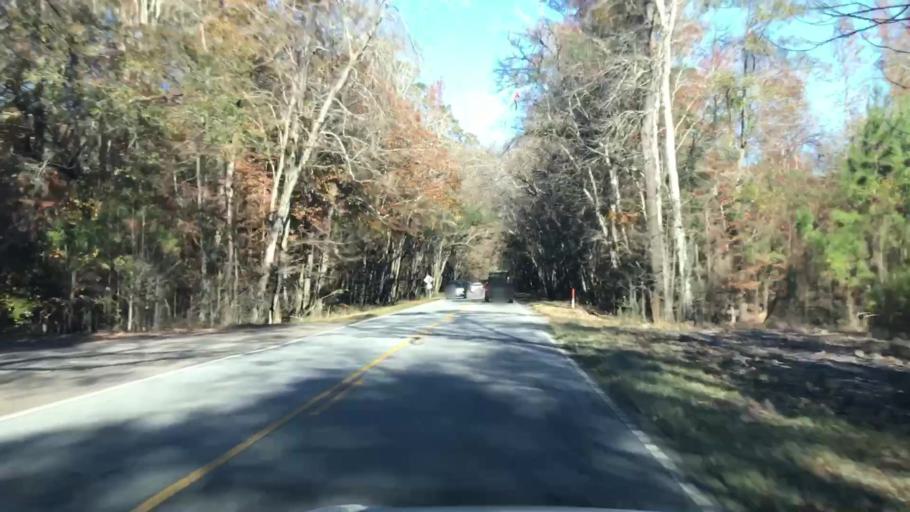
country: US
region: South Carolina
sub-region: Berkeley County
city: Ladson
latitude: 32.9058
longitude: -80.1469
